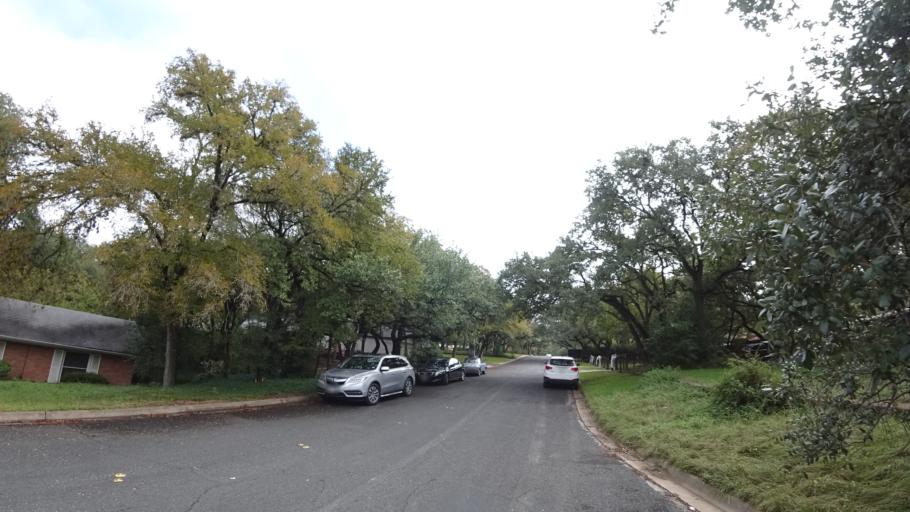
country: US
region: Texas
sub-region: Travis County
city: Rollingwood
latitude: 30.2563
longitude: -97.7779
